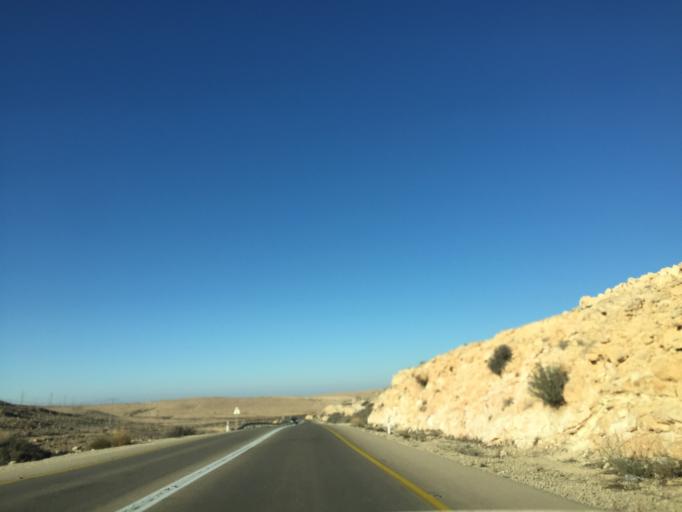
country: IL
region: Southern District
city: Mitzpe Ramon
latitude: 30.6993
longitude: 34.7837
